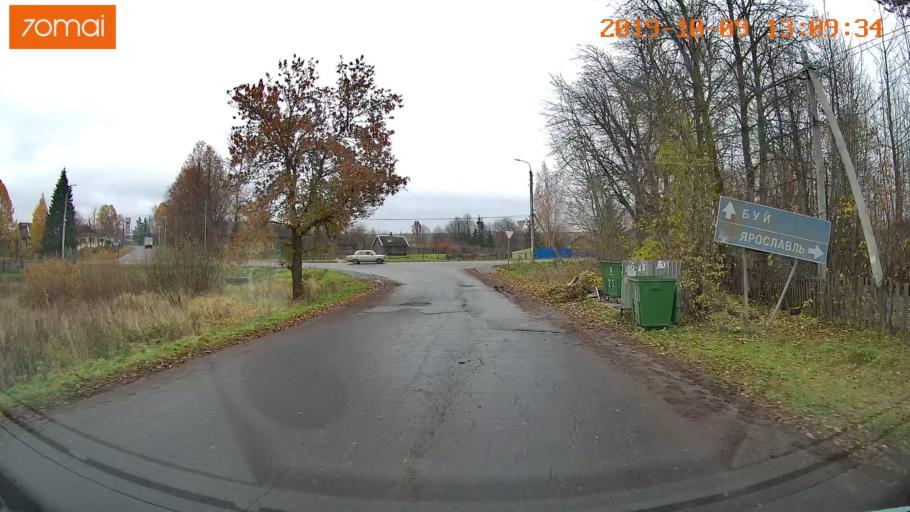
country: RU
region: Jaroslavl
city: Lyubim
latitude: 58.3557
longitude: 40.6766
